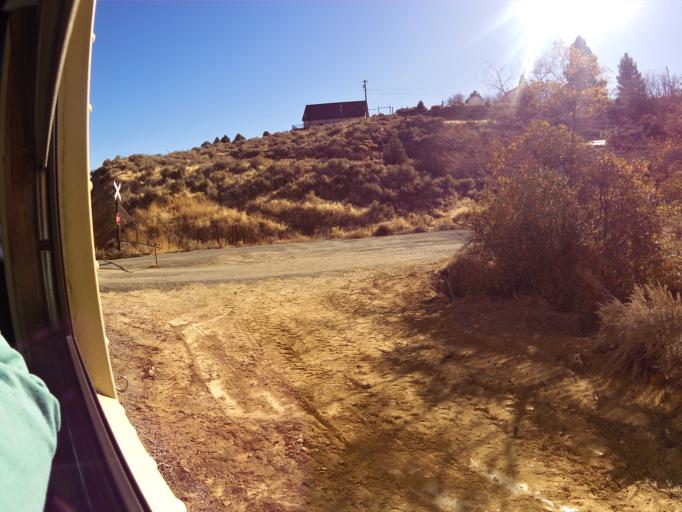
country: US
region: Nevada
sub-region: Storey County
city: Virginia City
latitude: 39.3017
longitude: -119.6502
